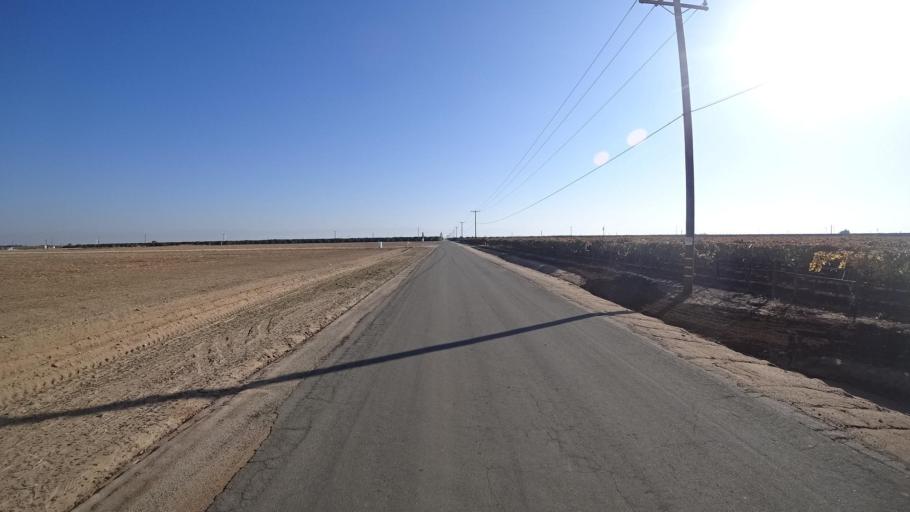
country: US
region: California
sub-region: Tulare County
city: Richgrove
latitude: 35.7327
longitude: -119.1457
